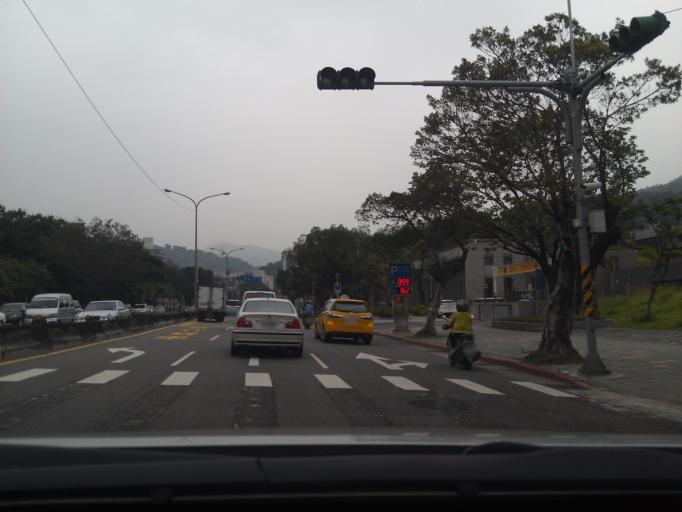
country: TW
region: Taipei
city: Taipei
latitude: 25.0961
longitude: 121.5302
